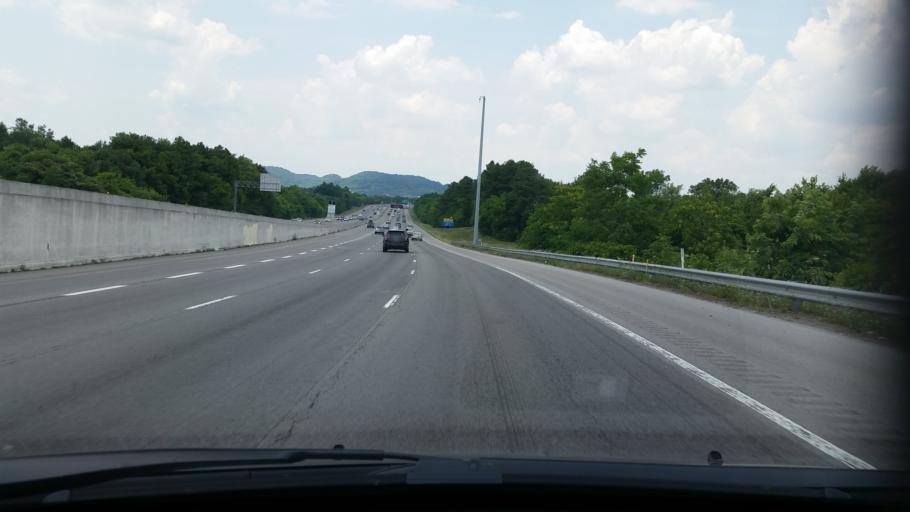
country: US
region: Tennessee
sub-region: Williamson County
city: Brentwood Estates
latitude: 36.0124
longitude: -86.7848
